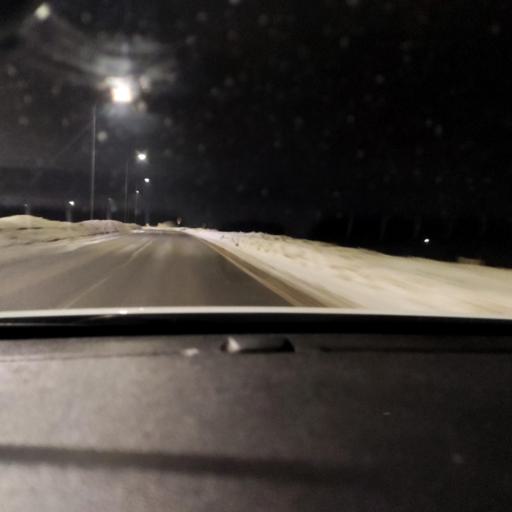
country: RU
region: Tatarstan
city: Sviyazhsk
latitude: 55.7415
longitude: 48.7767
